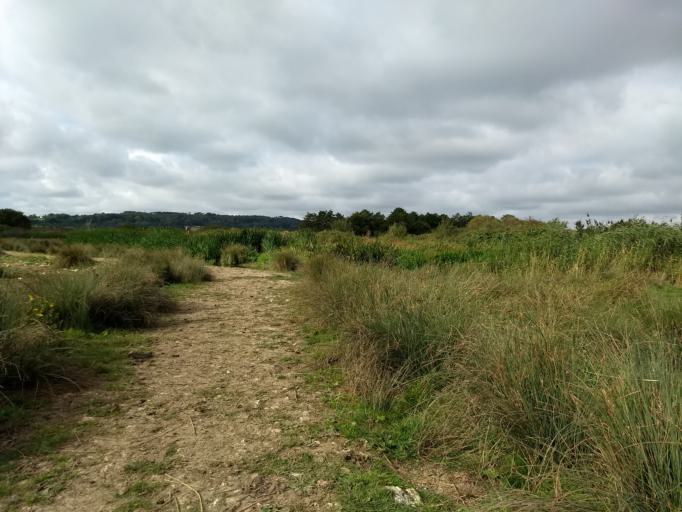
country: GB
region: England
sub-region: Isle of Wight
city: Brading
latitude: 50.6900
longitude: -1.1283
